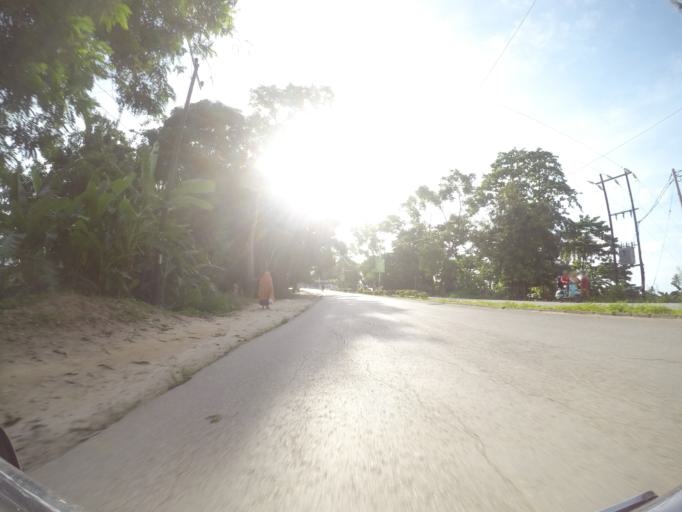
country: TZ
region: Pemba South
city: Chake Chake
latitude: -5.2371
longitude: 39.7758
